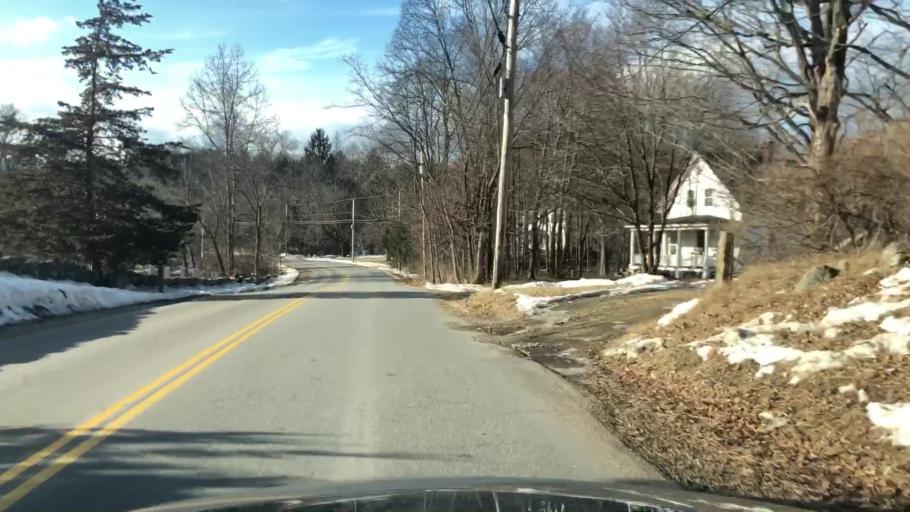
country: US
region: New Hampshire
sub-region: Hillsborough County
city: Milford
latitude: 42.8490
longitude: -71.6772
